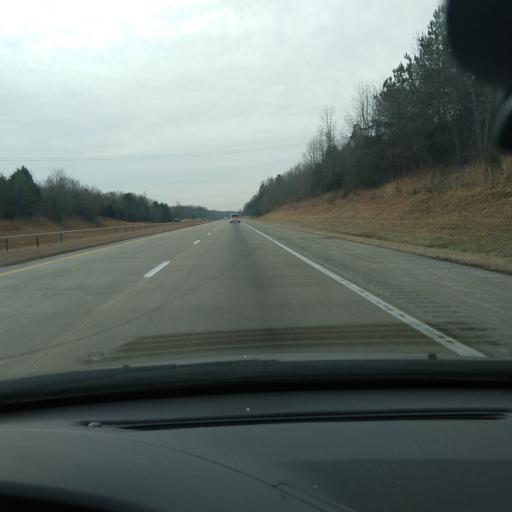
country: US
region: North Carolina
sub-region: Davidson County
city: Welcome
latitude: 35.9002
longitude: -80.2341
